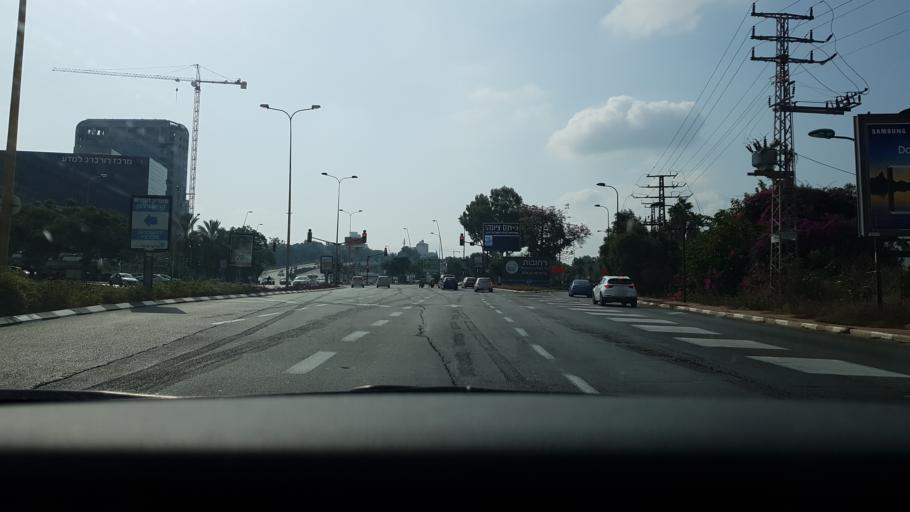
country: IL
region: Central District
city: Ness Ziona
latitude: 31.9126
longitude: 34.8023
